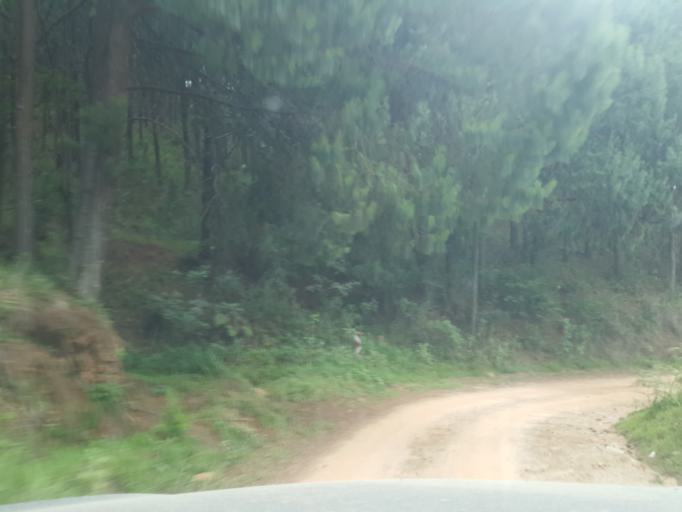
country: ZA
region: Limpopo
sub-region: Mopani District Municipality
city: Hoedspruit
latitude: -24.5895
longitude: 30.8689
